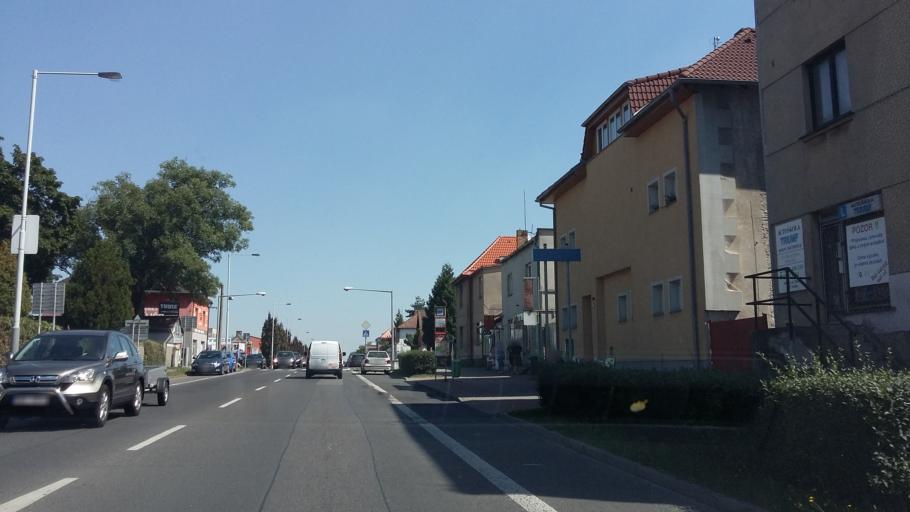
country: CZ
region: Praha
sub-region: Praha 20
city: Horni Pocernice
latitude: 50.1137
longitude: 14.6029
